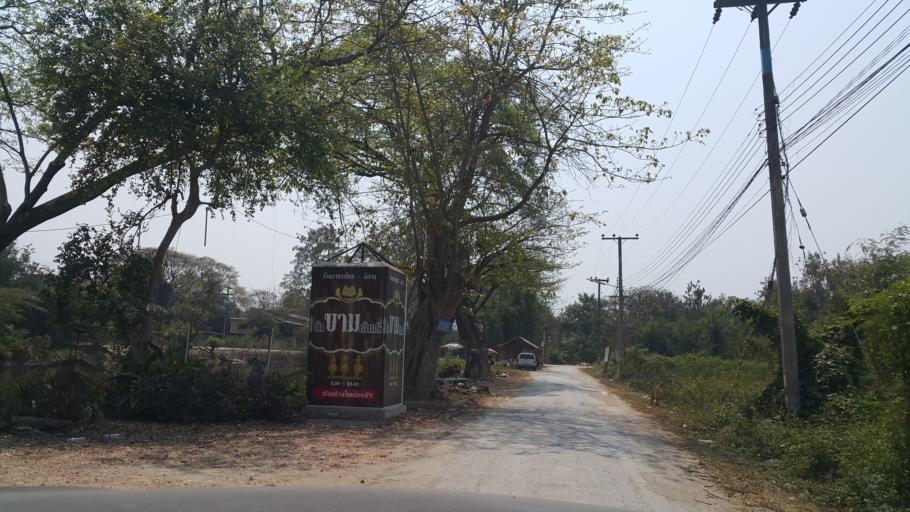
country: TH
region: Chiang Mai
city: Saraphi
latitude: 18.7644
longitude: 99.0341
